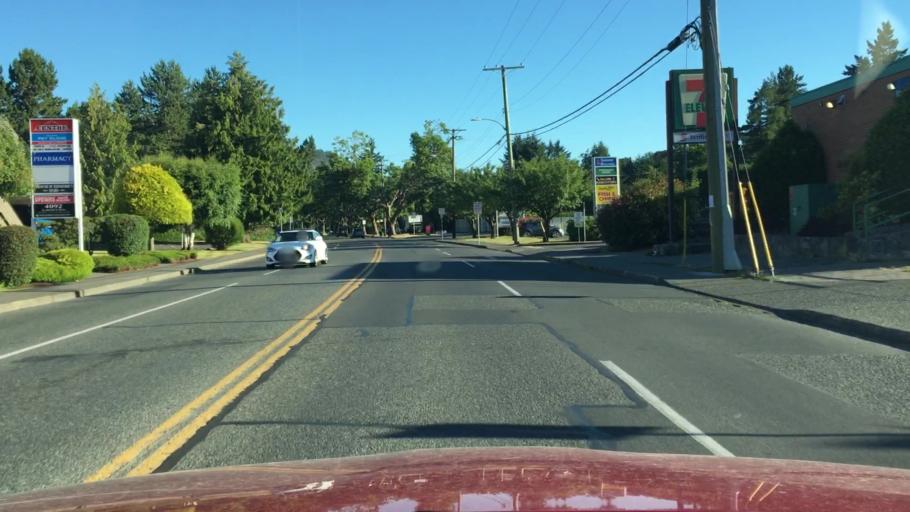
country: CA
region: British Columbia
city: Oak Bay
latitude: 48.4764
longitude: -123.3330
